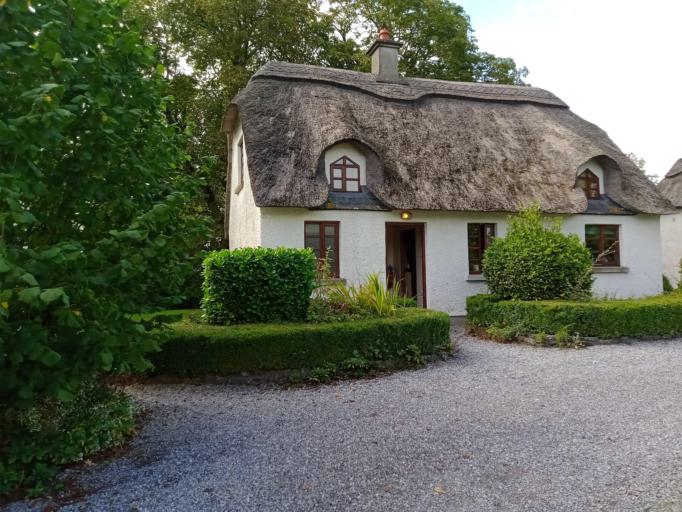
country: IE
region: Leinster
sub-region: Kilkenny
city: Kilkenny
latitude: 52.6147
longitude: -7.2092
